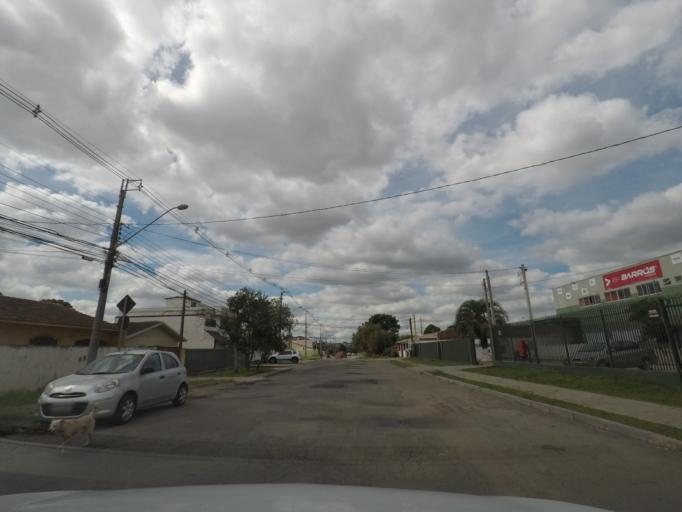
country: BR
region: Parana
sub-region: Sao Jose Dos Pinhais
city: Sao Jose dos Pinhais
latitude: -25.4929
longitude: -49.2387
